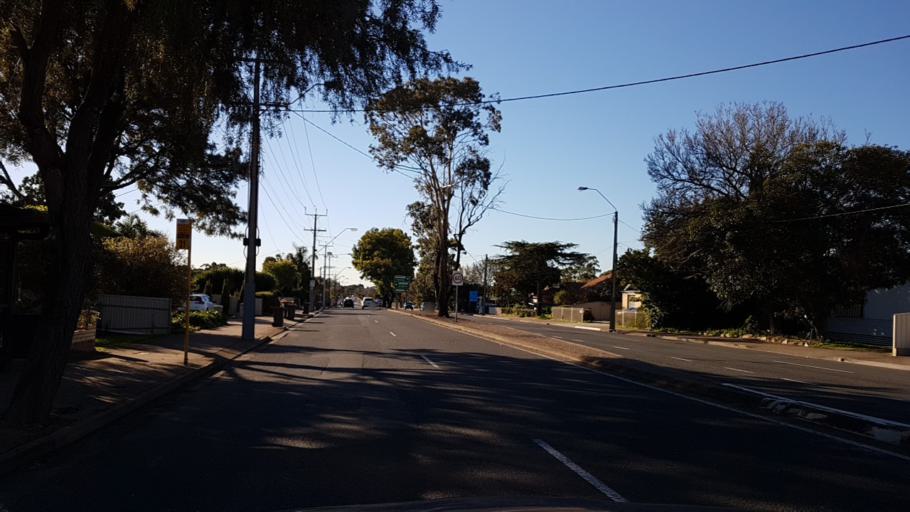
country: AU
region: South Australia
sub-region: Marion
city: Sturt
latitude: -35.0208
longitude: 138.5498
